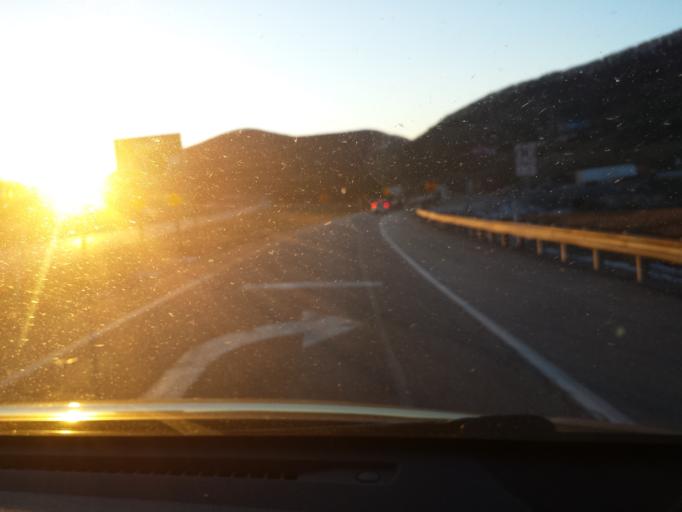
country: US
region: Pennsylvania
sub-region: Centre County
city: Zion
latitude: 40.9459
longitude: -77.7144
